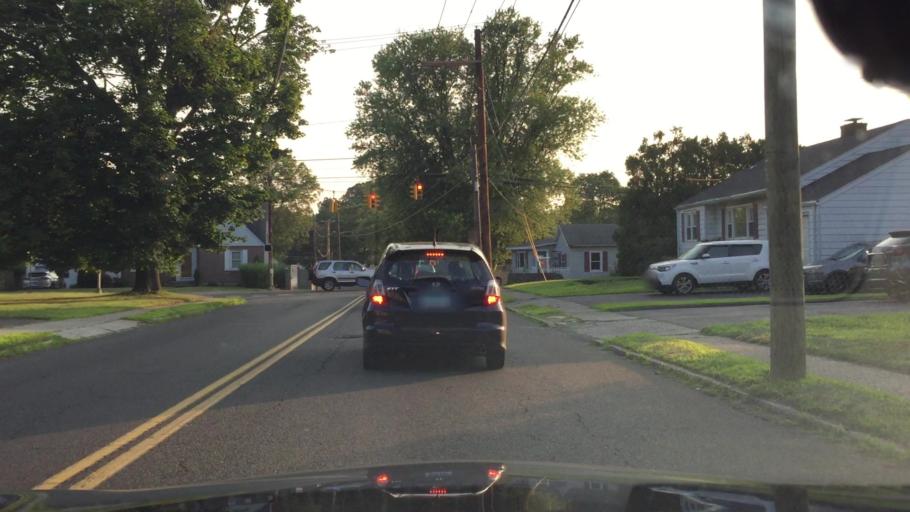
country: US
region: Connecticut
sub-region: New Haven County
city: City of Milford (balance)
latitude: 41.2064
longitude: -73.0811
